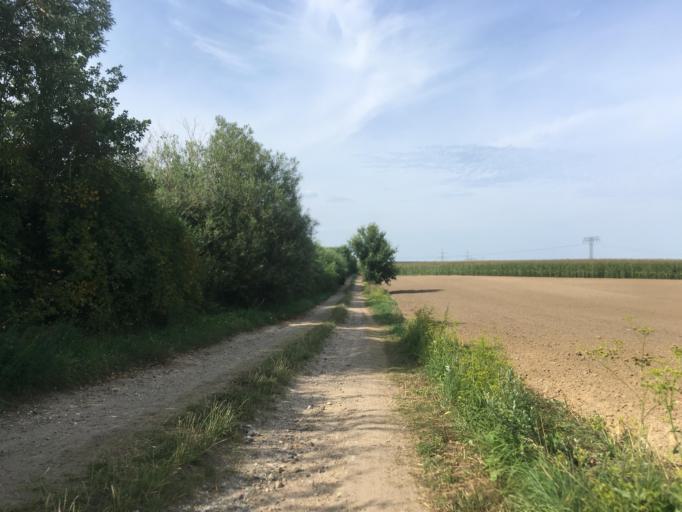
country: DE
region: Brandenburg
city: Melchow
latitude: 52.7205
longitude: 13.7251
